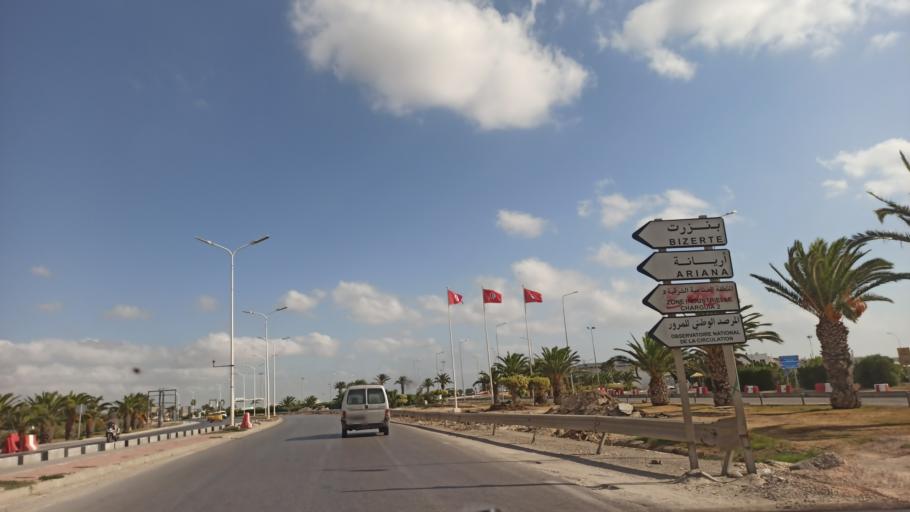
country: TN
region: Ariana
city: Ariana
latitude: 36.8436
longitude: 10.2151
